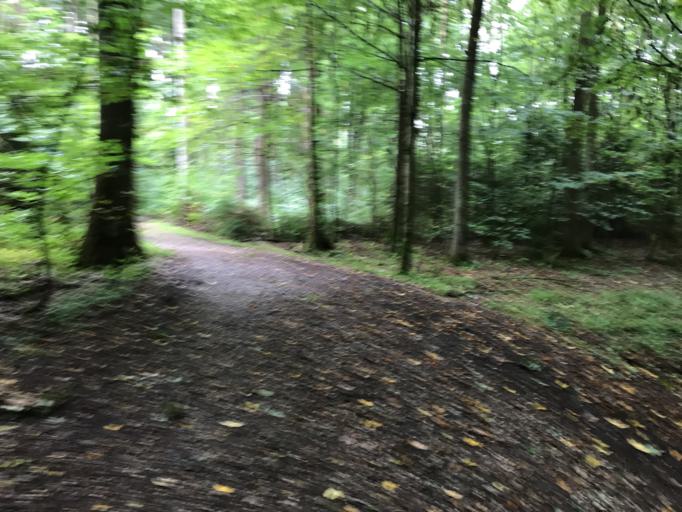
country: DE
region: Bavaria
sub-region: Upper Bavaria
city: Grunwald
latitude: 48.0225
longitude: 11.5340
